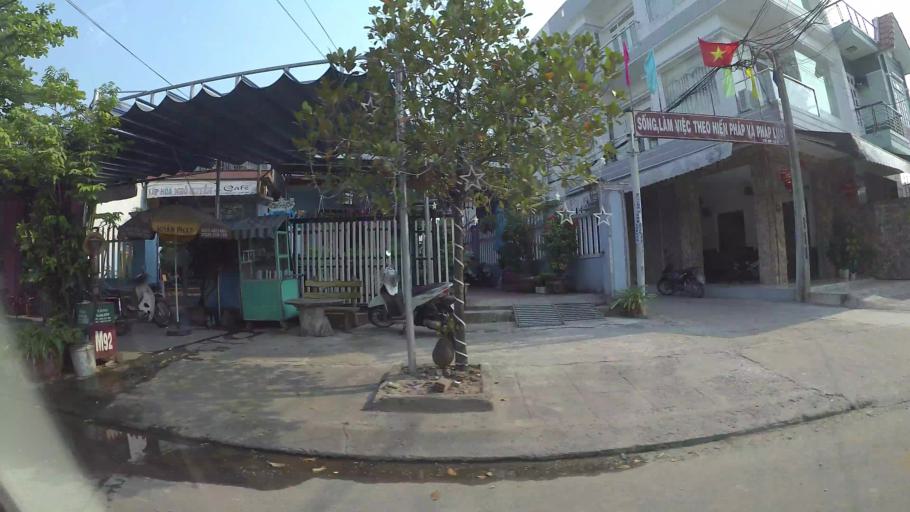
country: VN
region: Da Nang
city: Lien Chieu
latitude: 16.0487
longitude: 108.1727
